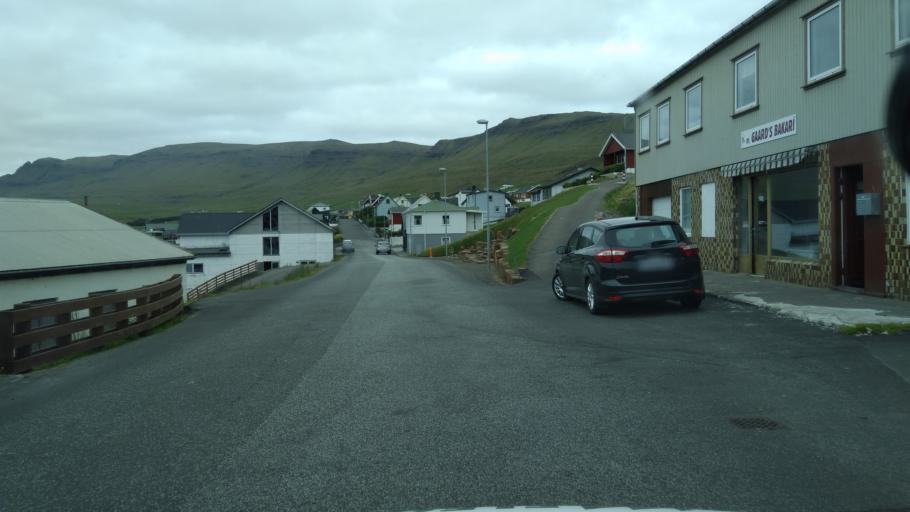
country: FO
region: Suduroy
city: Tvoroyri
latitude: 61.5618
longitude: -6.8292
